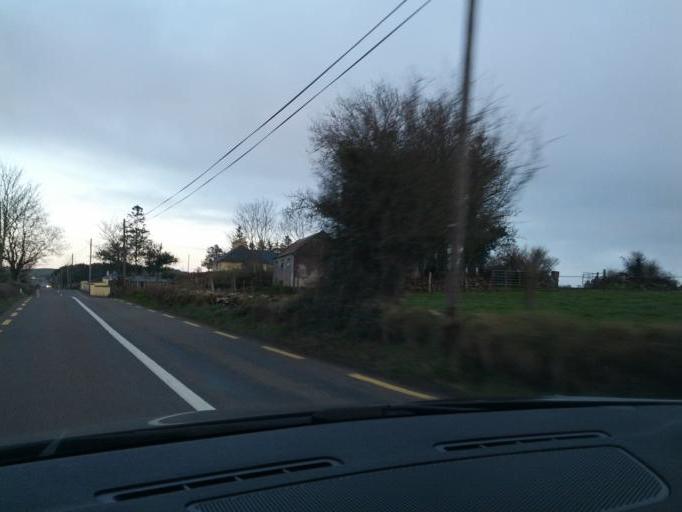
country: IE
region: Connaught
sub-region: Sligo
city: Ballymote
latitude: 53.9868
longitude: -8.4839
